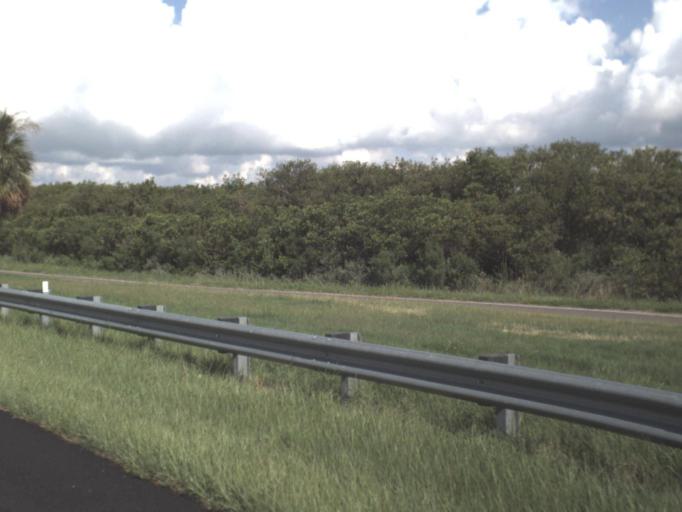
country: US
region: Florida
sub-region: Hillsborough County
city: Town 'n' Country
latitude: 27.9727
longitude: -82.6019
